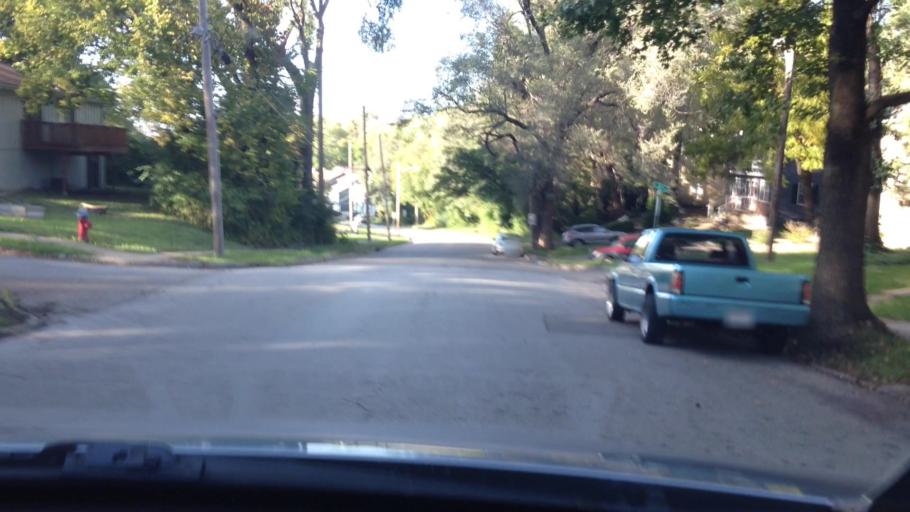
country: US
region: Kansas
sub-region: Johnson County
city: Westwood
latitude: 39.0636
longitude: -94.6072
